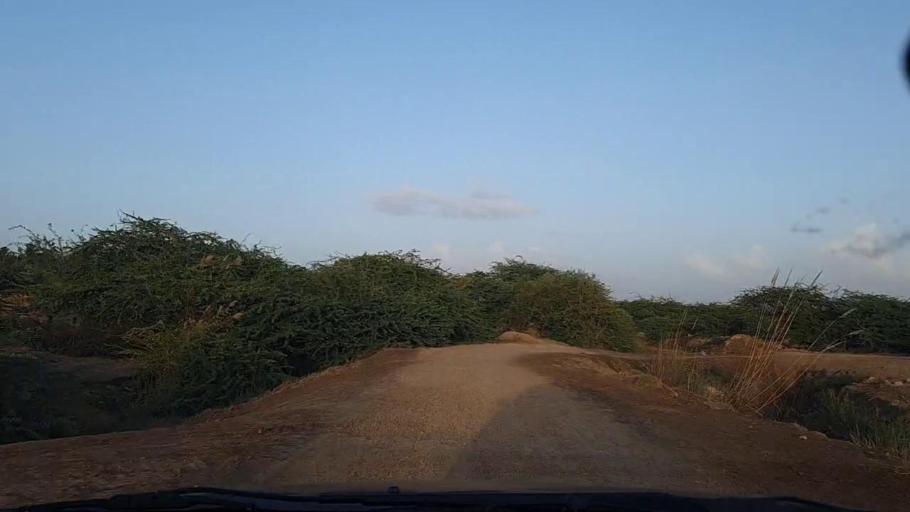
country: PK
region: Sindh
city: Keti Bandar
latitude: 24.1626
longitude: 67.6001
